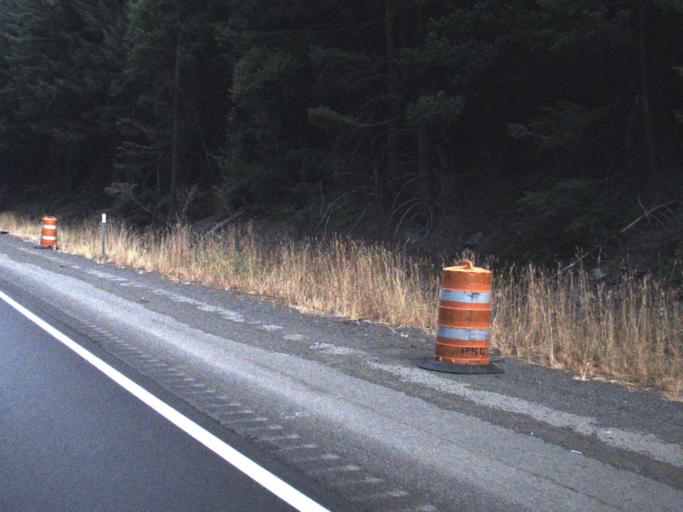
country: US
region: Washington
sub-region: Kittitas County
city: Cle Elum
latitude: 47.2761
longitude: -121.2765
